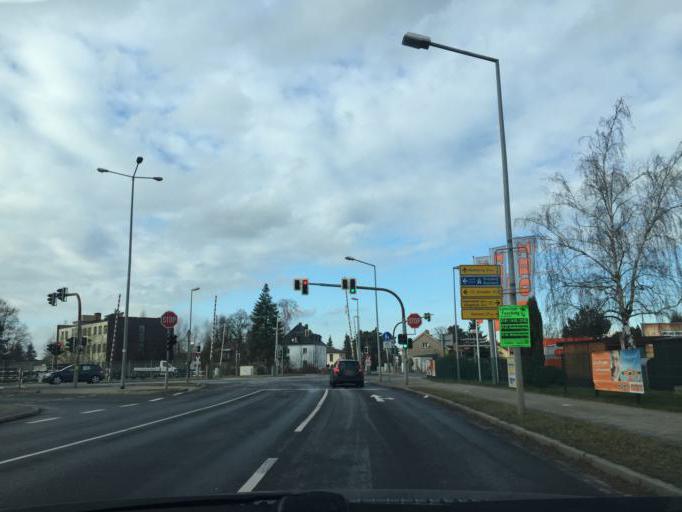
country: DE
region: Saxony
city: Ottendorf-Okrilla
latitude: 51.1763
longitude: 13.8258
